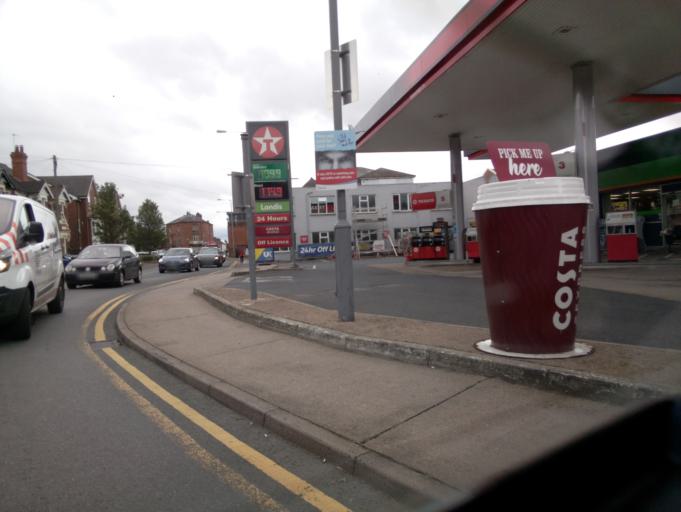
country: GB
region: England
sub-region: Worcestershire
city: Worcester
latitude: 52.1862
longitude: -2.2173
